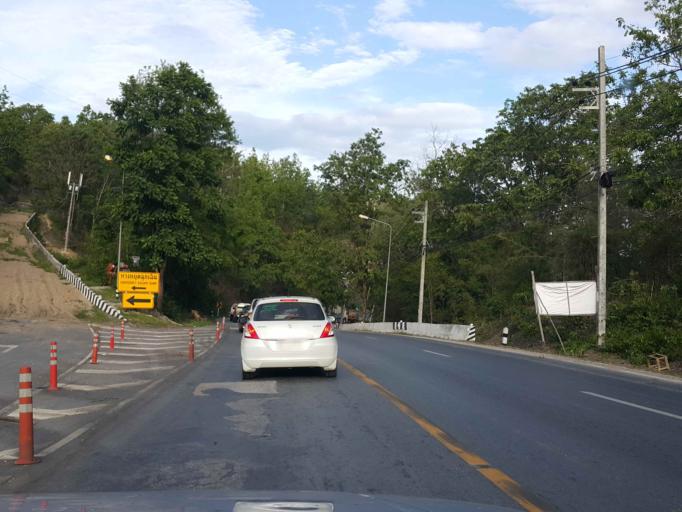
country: TH
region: Tak
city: Tak
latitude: 16.8133
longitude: 98.9754
